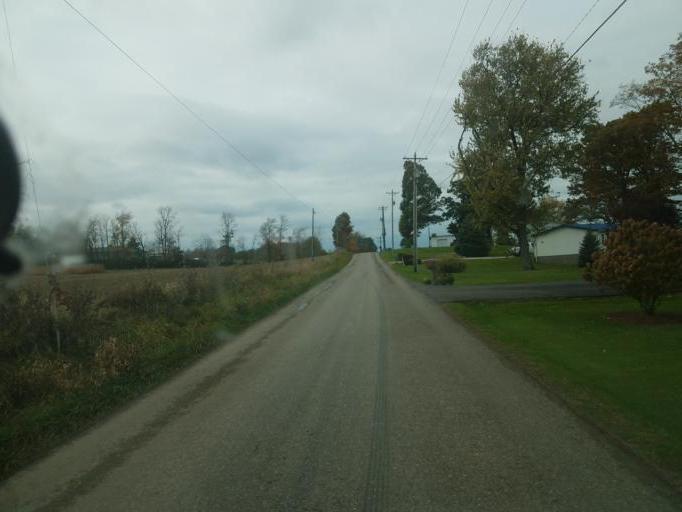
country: US
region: Ohio
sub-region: Wayne County
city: Shreve
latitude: 40.6243
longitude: -82.0920
